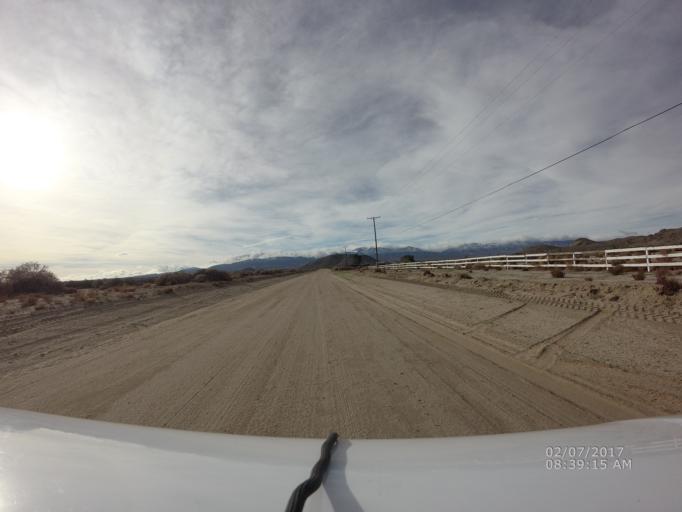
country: US
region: California
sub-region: Los Angeles County
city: Lake Los Angeles
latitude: 34.5914
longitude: -117.7200
